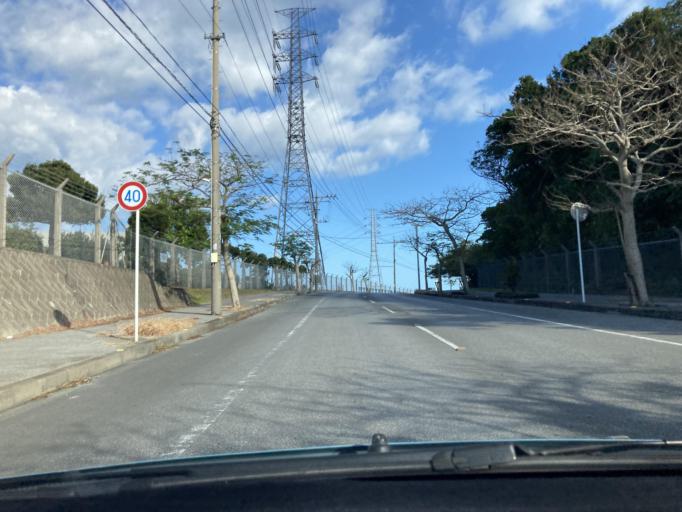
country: JP
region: Okinawa
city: Gushikawa
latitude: 26.3862
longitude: 127.8610
